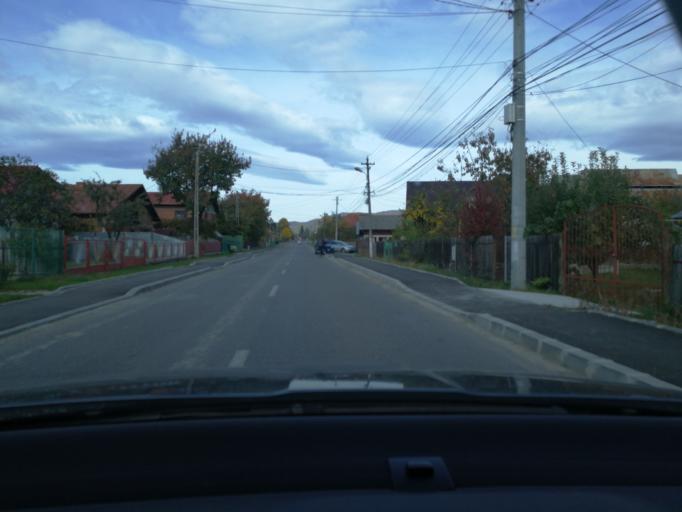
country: RO
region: Prahova
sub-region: Comuna Brebu
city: Brebu Megiesesc
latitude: 45.1645
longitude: 25.7742
